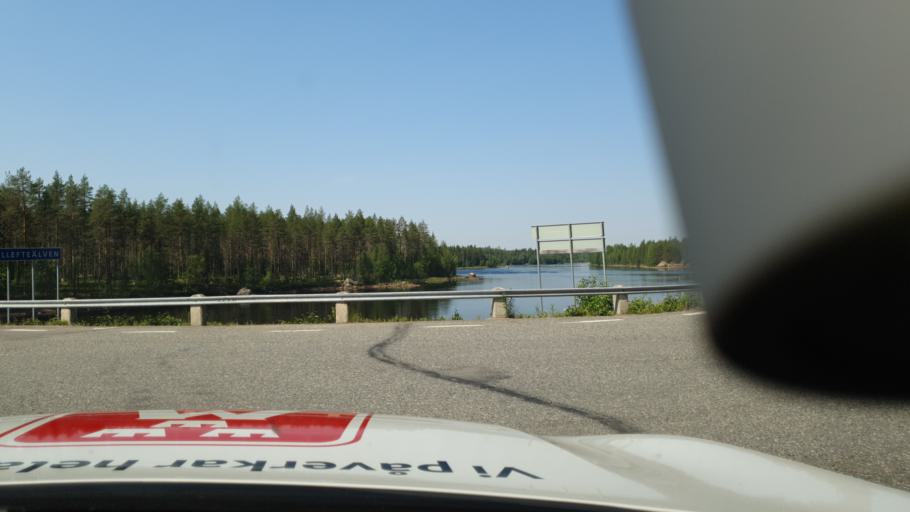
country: SE
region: Vaesterbotten
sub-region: Skelleftea Kommun
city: Langsele
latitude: 64.9627
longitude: 19.8896
